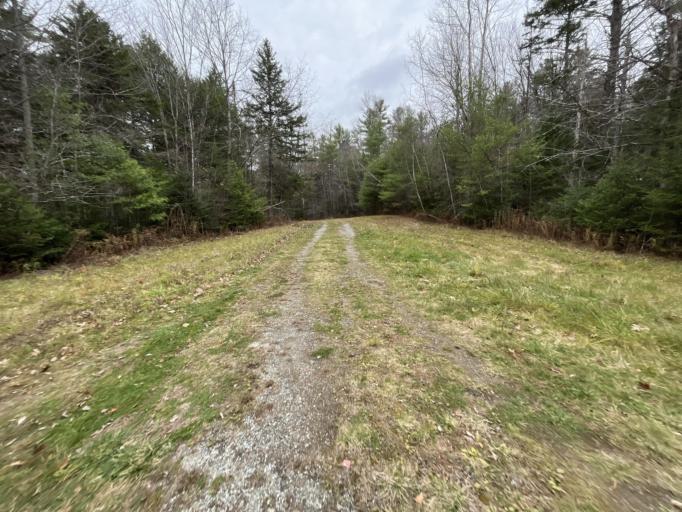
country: US
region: New Hampshire
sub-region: Merrimack County
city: New London
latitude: 43.4052
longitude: -71.9822
